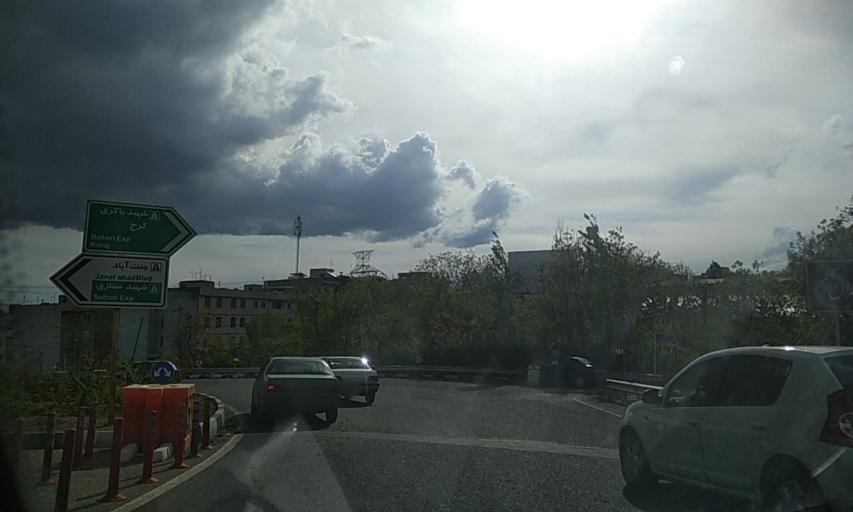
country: IR
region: Tehran
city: Tajrish
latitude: 35.7748
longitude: 51.2992
